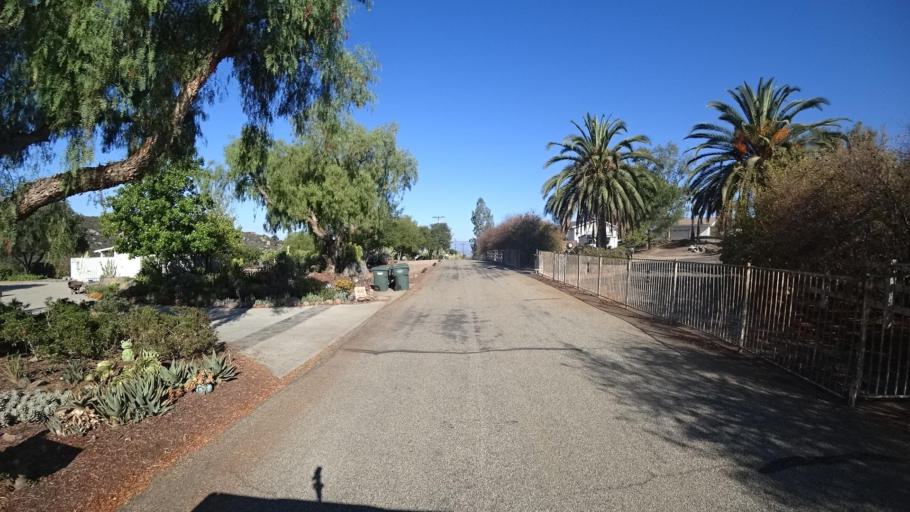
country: US
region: California
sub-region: San Diego County
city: Hidden Meadows
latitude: 33.2396
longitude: -117.1210
